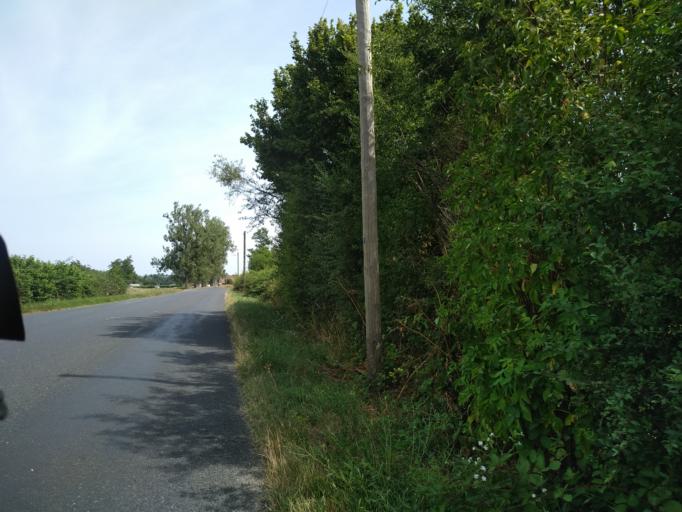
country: FR
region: Bourgogne
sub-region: Departement de Saone-et-Loire
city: Digoin
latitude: 46.4637
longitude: 3.9656
